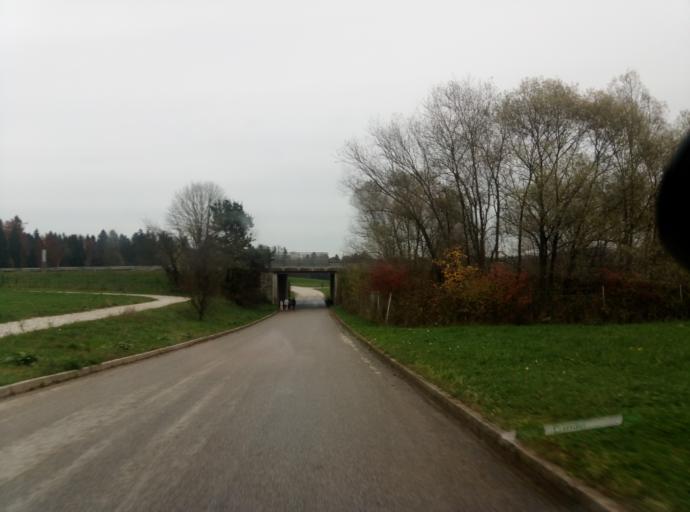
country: SI
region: Vodice
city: Vodice
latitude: 46.1770
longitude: 14.4848
